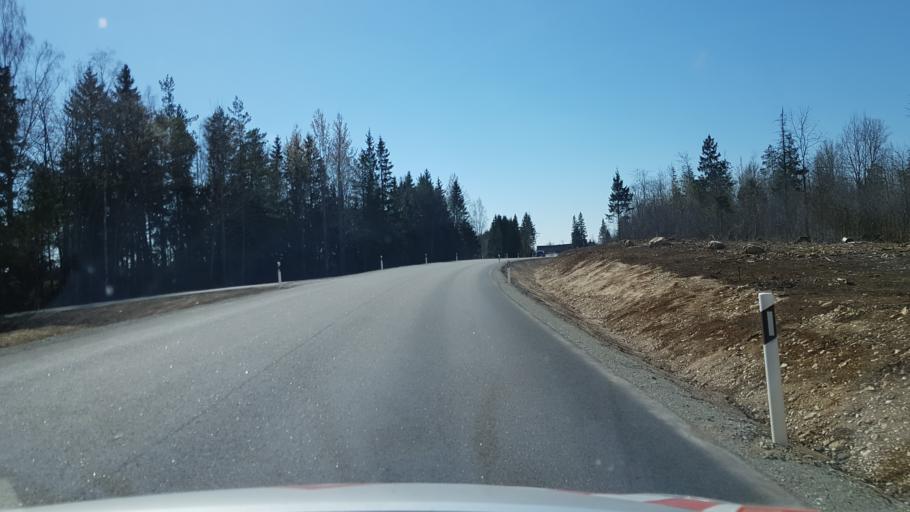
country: EE
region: Laeaene-Virumaa
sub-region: Vinni vald
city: Vinni
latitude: 59.1196
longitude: 26.6180
